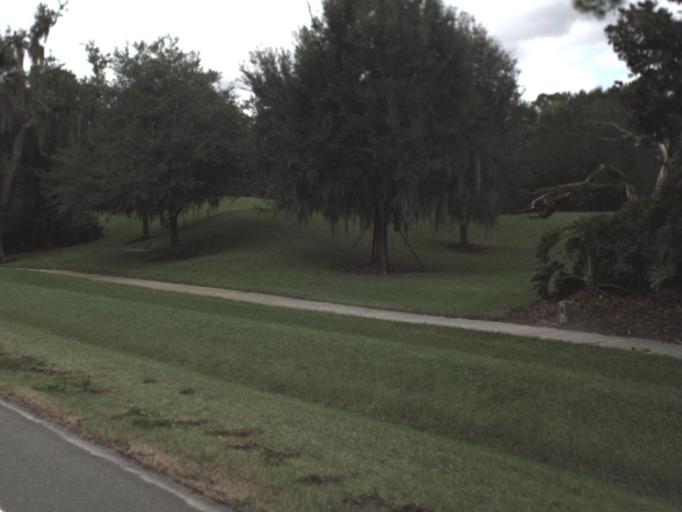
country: US
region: Florida
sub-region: Sarasota County
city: Desoto Lakes
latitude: 27.3885
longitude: -82.4742
